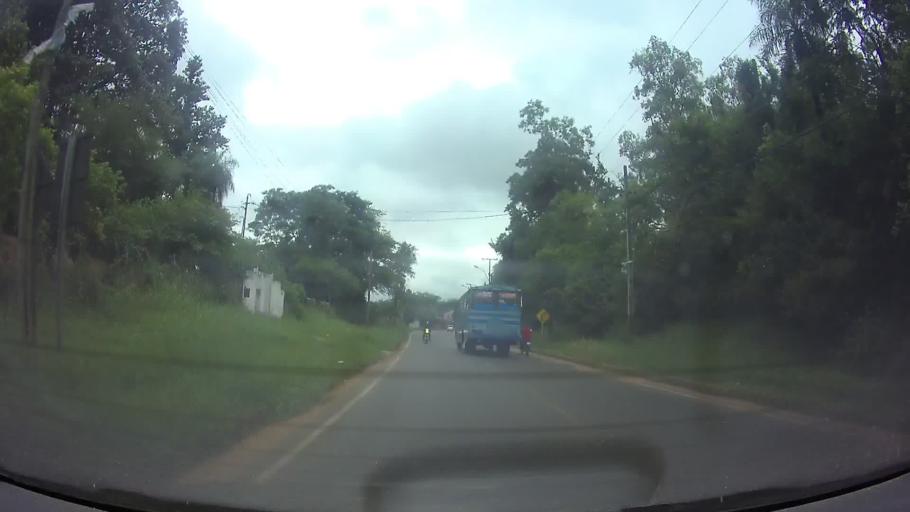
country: PY
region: Central
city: Nemby
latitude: -25.3819
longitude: -57.5471
